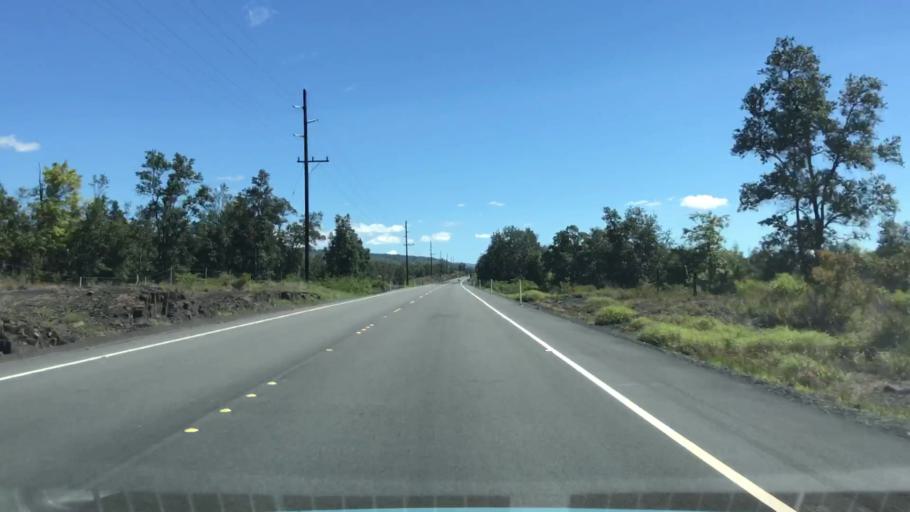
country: US
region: Hawaii
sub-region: Hawaii County
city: Pahala
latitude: 19.3356
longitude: -155.3958
